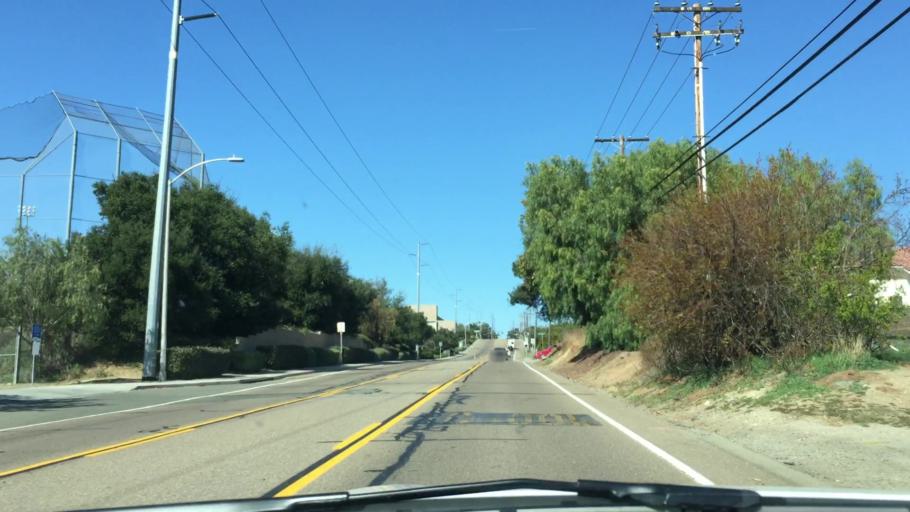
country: US
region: California
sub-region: San Diego County
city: Valley Center
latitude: 33.2757
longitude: -117.0235
